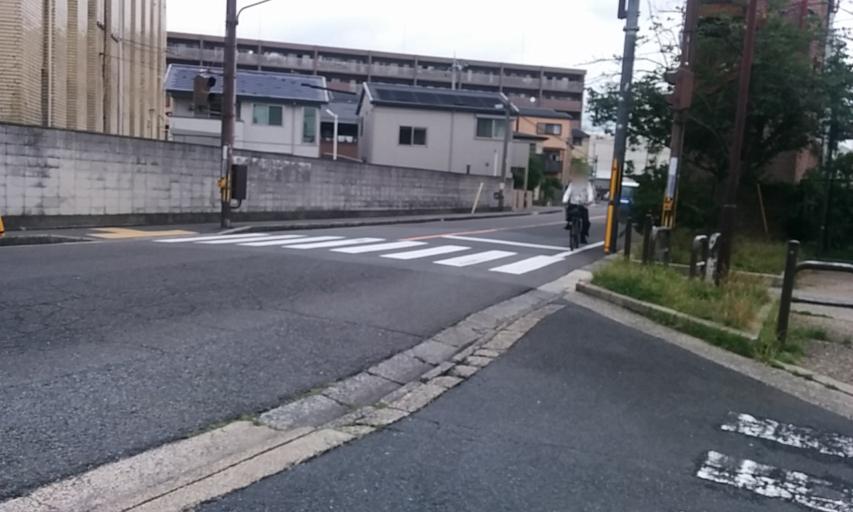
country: JP
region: Kyoto
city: Kyoto
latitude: 34.9865
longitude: 135.7409
